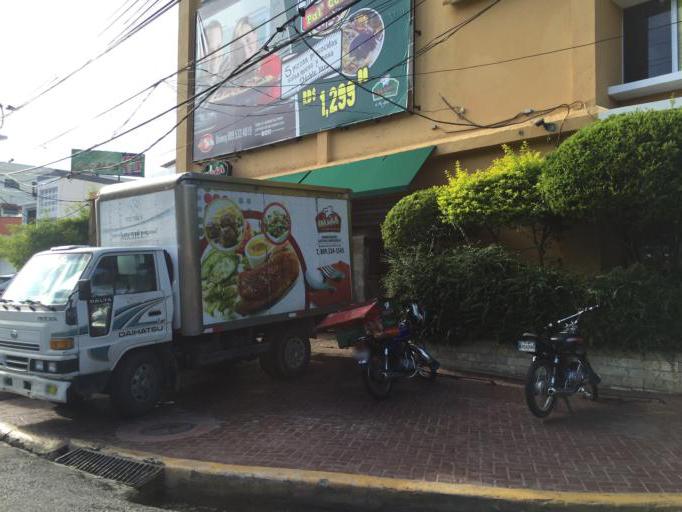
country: DO
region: Nacional
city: La Julia
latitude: 18.4623
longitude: -69.9196
